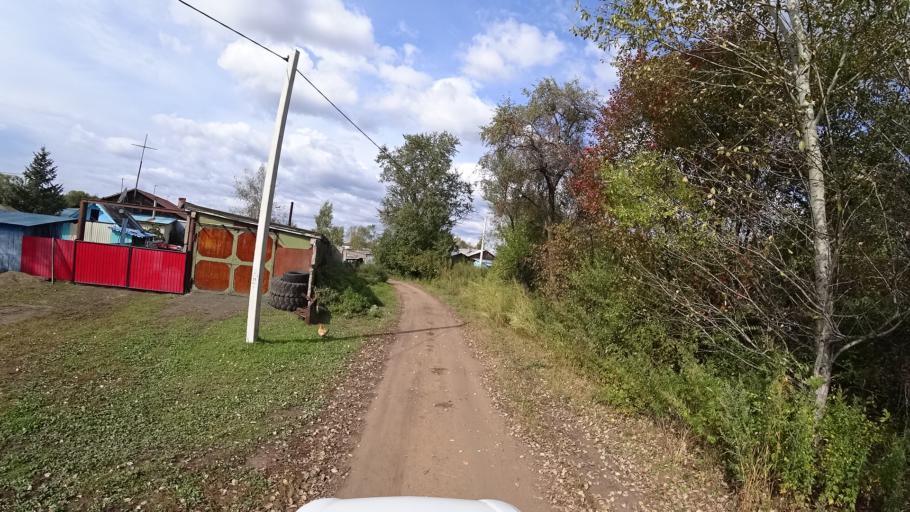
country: RU
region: Amur
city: Arkhara
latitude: 49.3522
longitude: 130.1594
